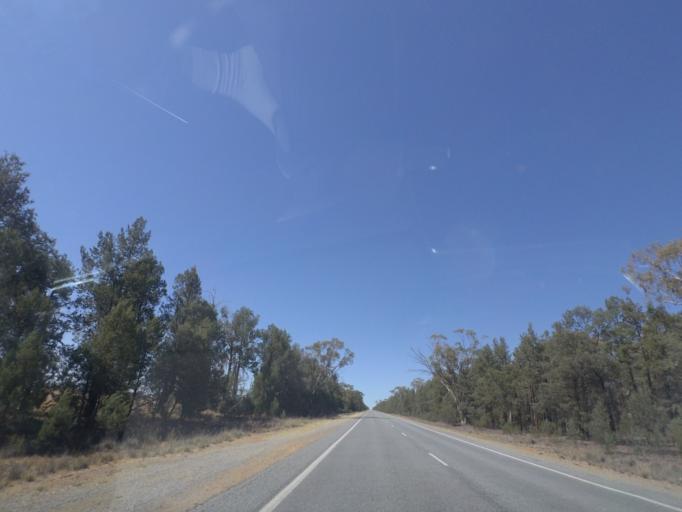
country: AU
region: New South Wales
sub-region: Narrandera
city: Narrandera
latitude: -34.4239
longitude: 146.8445
